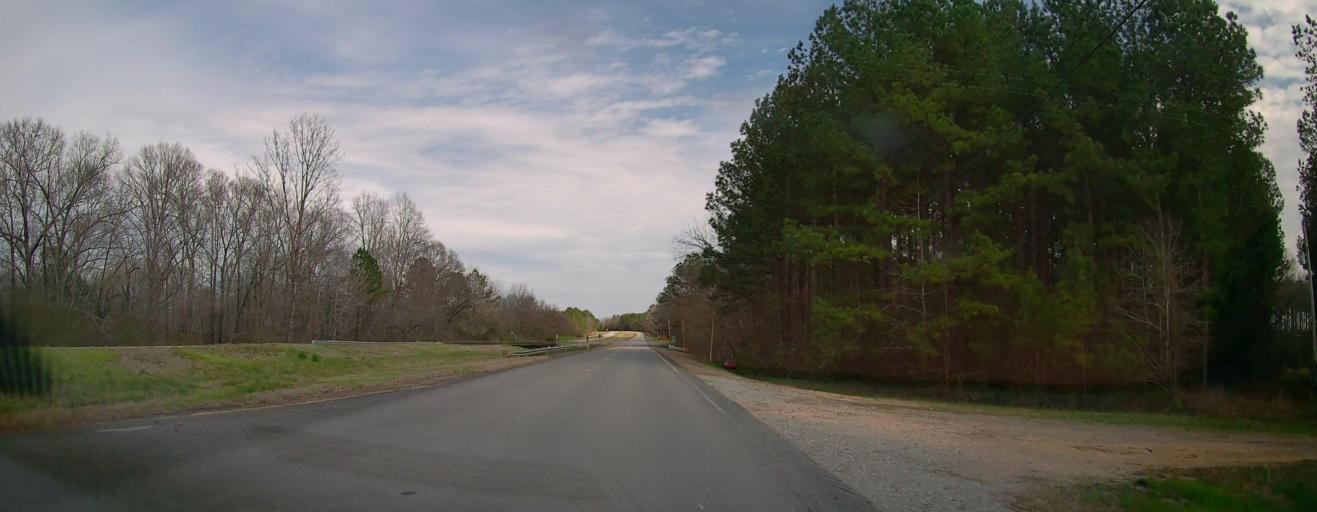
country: US
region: Alabama
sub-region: Marion County
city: Winfield
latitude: 33.9299
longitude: -87.6817
